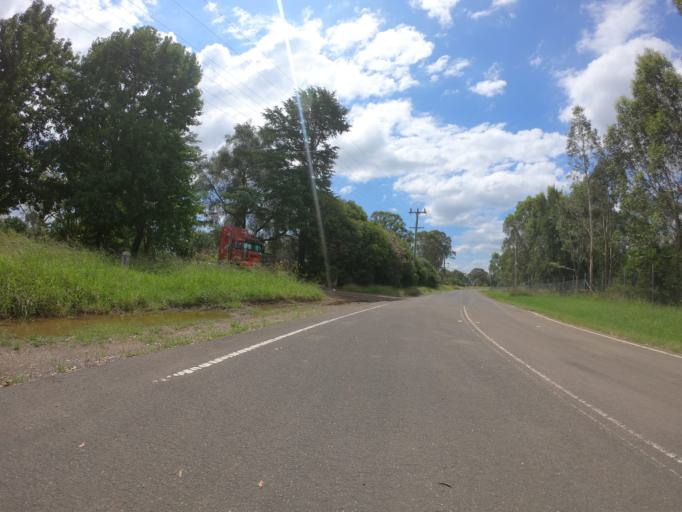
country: AU
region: New South Wales
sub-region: Blacktown
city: Mount Druitt
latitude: -33.8041
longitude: 150.7676
